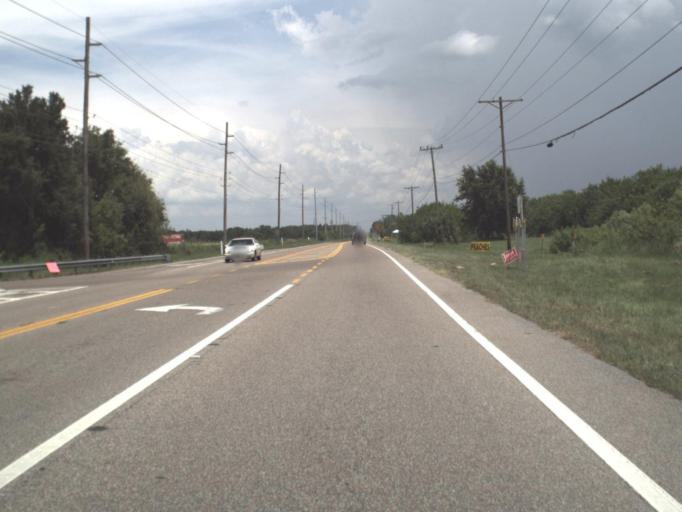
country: US
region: Florida
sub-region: Hillsborough County
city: Sun City Center
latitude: 27.7405
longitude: -82.3352
